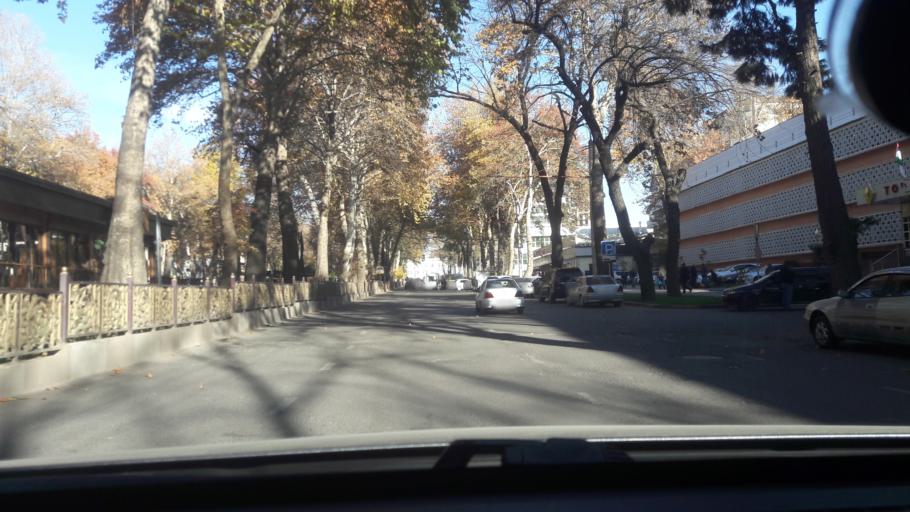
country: TJ
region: Dushanbe
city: Dushanbe
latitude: 38.5594
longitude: 68.7997
